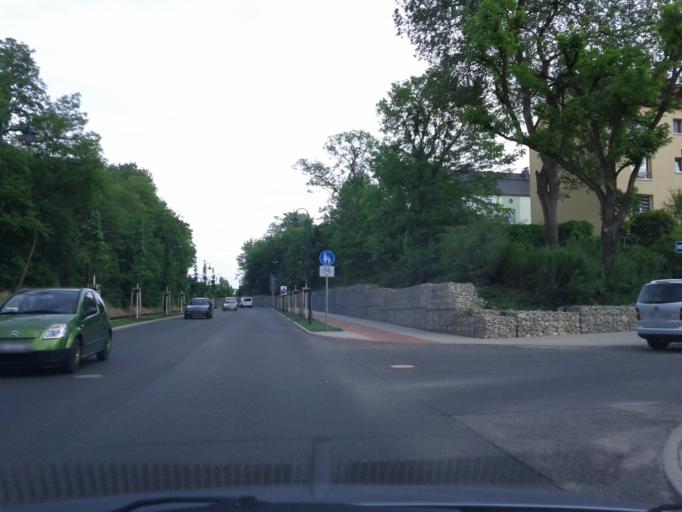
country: DE
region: Brandenburg
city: Woltersdorf
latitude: 52.4730
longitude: 13.7766
